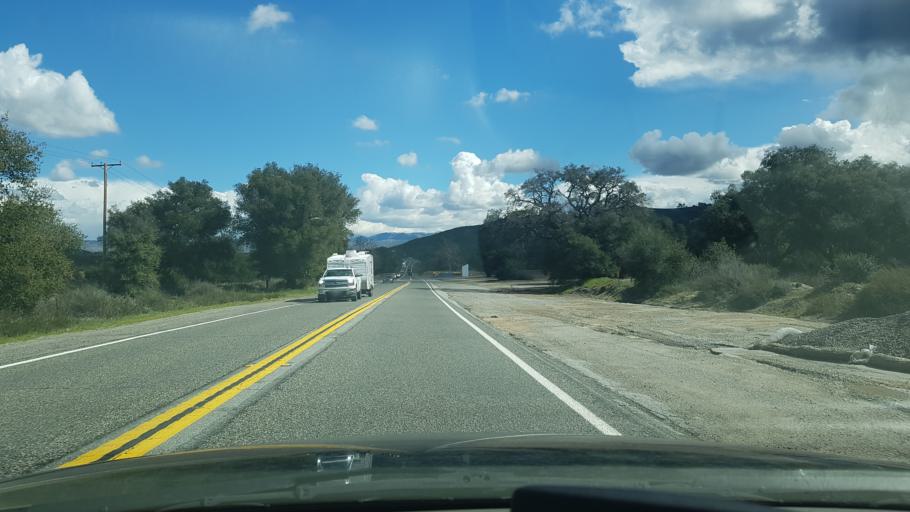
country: US
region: California
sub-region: Riverside County
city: Aguanga
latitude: 33.4684
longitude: -117.0016
